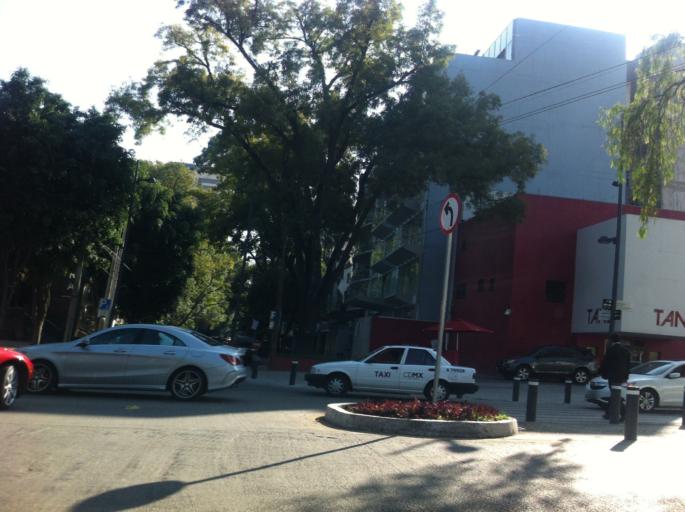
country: MX
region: Mexico City
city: Miguel Hidalgo
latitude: 19.4322
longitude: -99.1999
